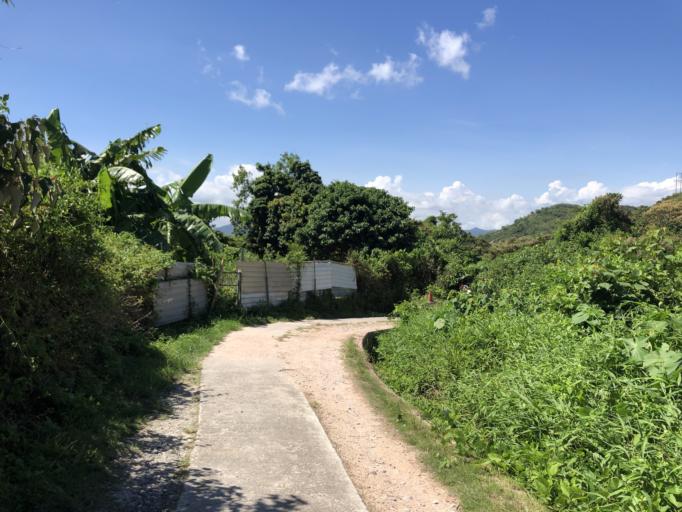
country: HK
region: Tuen Mun
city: Tuen Mun
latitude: 22.2905
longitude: 113.9788
